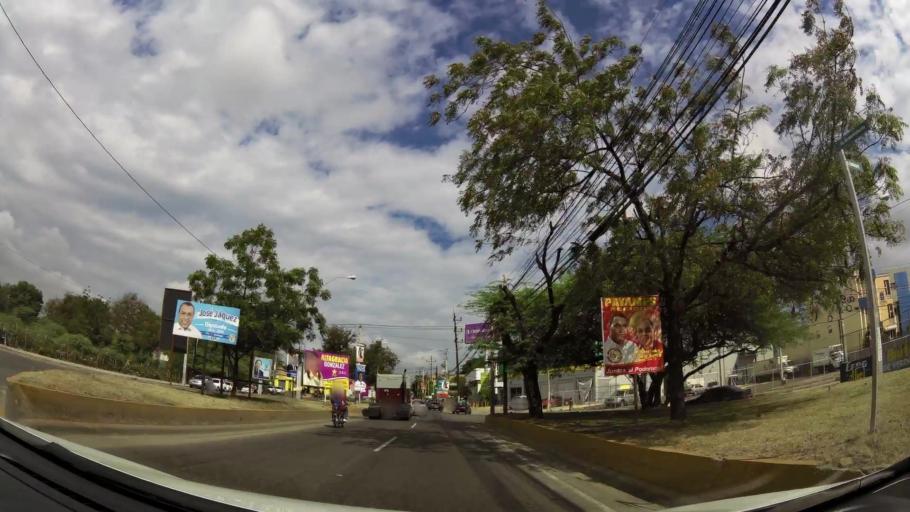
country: DO
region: Santiago
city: Santiago de los Caballeros
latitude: 19.4787
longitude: -70.7254
